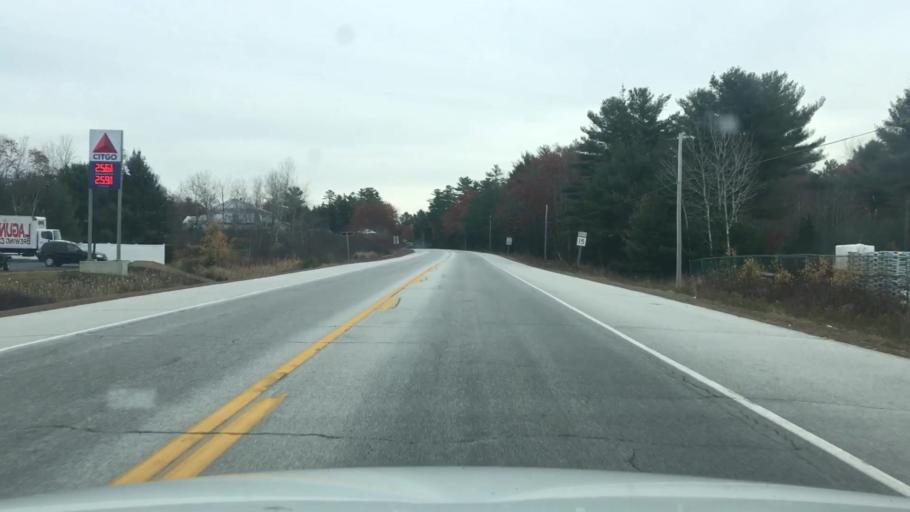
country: US
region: Maine
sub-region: Hancock County
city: Orland
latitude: 44.5701
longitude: -68.7645
